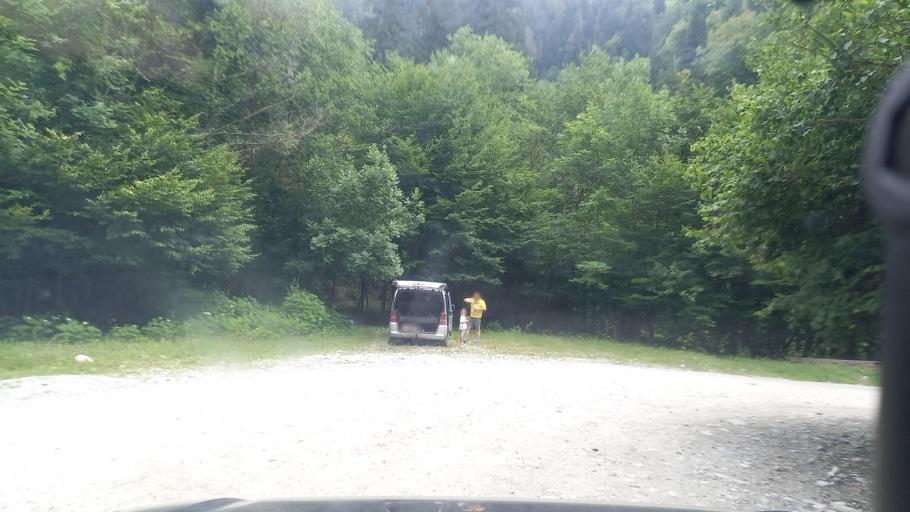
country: RU
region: Karachayevo-Cherkesiya
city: Kurdzhinovo
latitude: 43.8880
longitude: 40.9499
